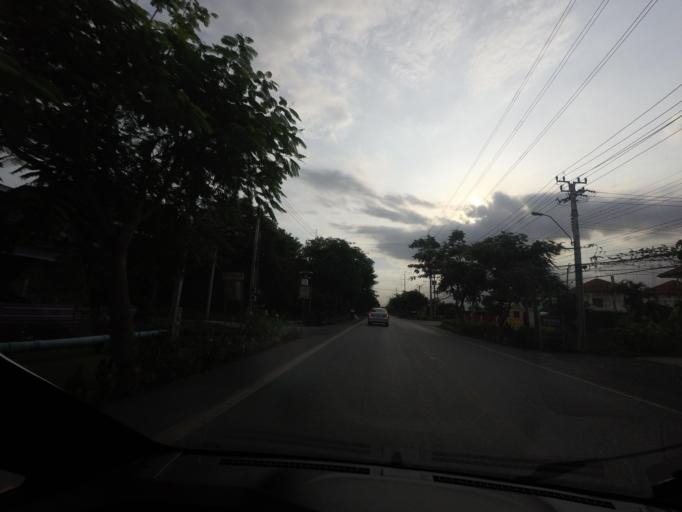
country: TH
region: Bangkok
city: Nong Chok
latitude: 13.8594
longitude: 100.8580
